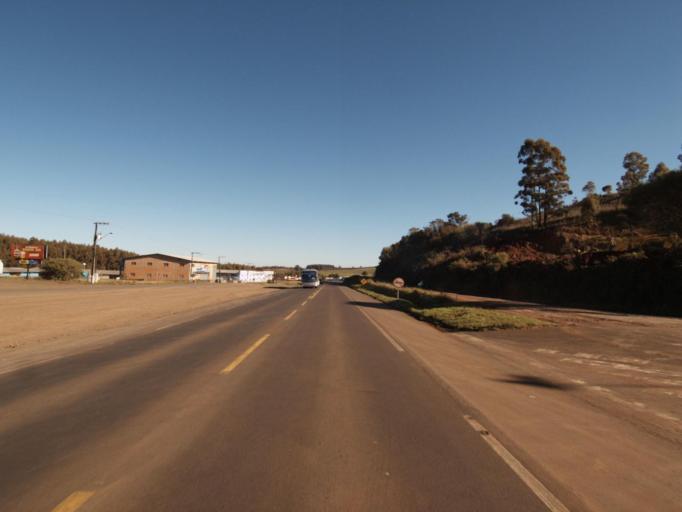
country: BR
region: Santa Catarina
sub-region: Chapeco
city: Chapeco
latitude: -26.9941
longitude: -52.6113
